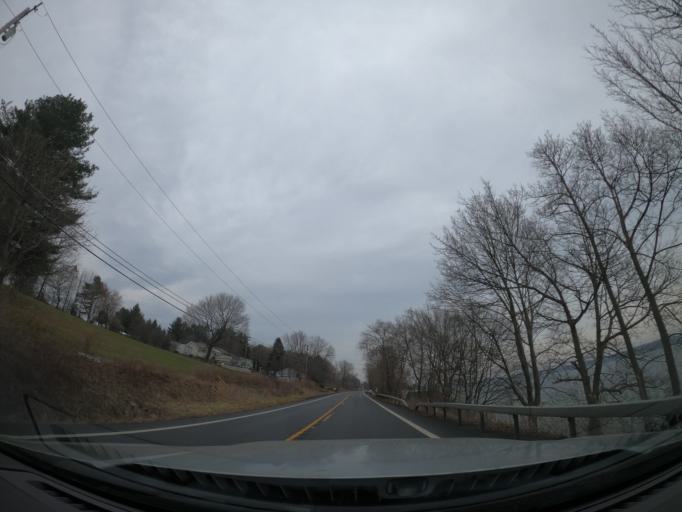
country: US
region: New York
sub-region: Cayuga County
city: Melrose Park
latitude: 42.8504
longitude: -76.5295
